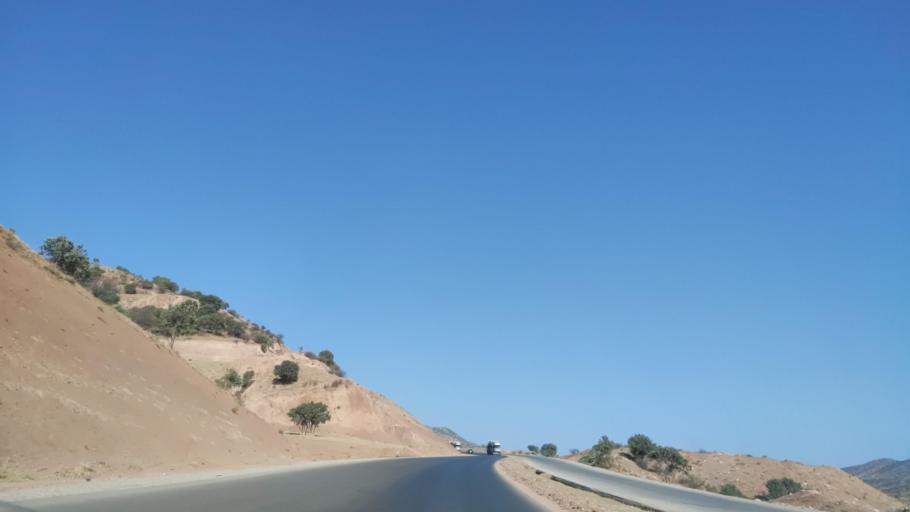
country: IQ
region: Arbil
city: Shaqlawah
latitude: 36.4317
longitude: 44.3133
